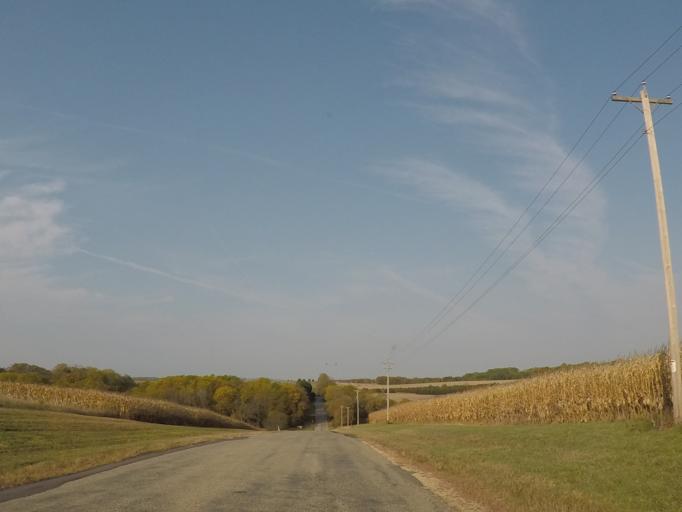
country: US
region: Wisconsin
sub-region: Dane County
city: Cross Plains
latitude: 43.0420
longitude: -89.6069
